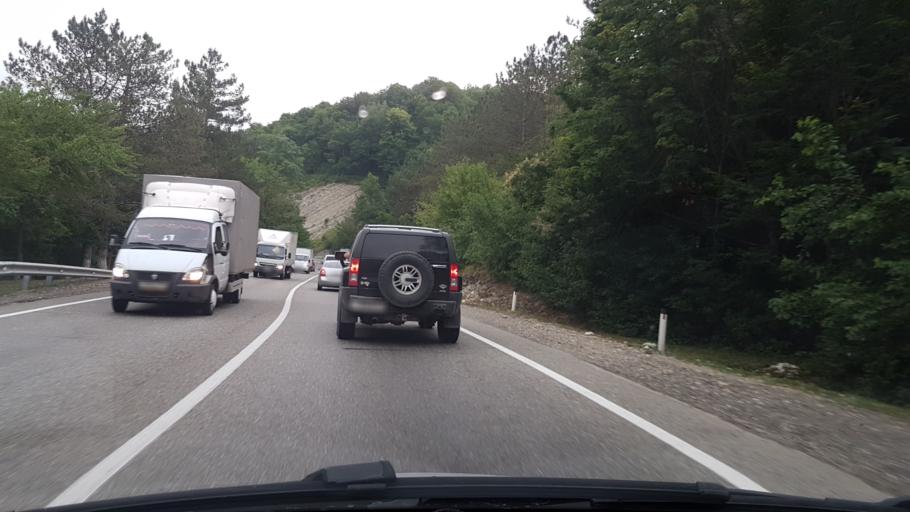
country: RU
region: Krasnodarskiy
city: Novomikhaylovskiy
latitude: 44.2476
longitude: 38.8853
